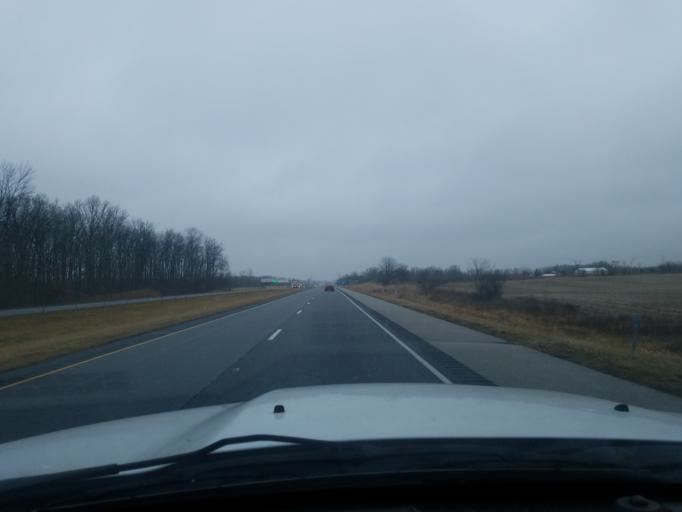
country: US
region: Indiana
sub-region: Grant County
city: Gas City
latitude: 40.5347
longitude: -85.5503
